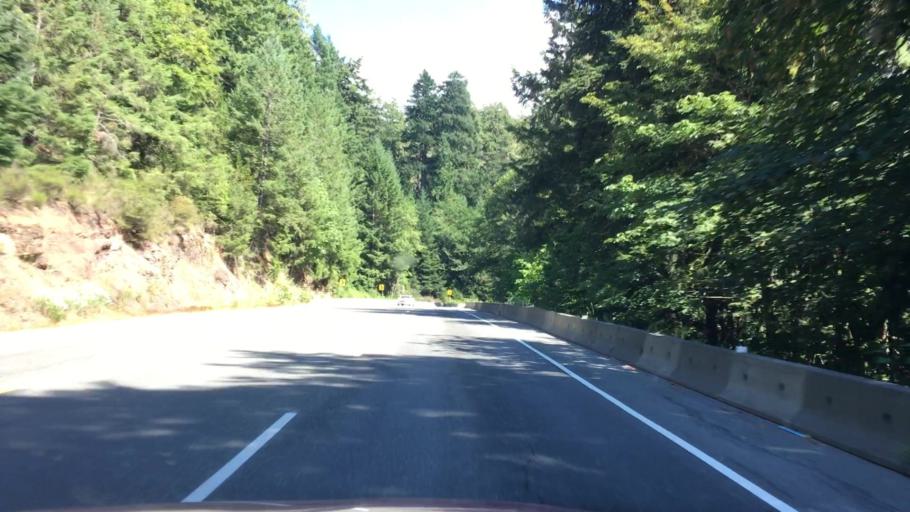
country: CA
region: British Columbia
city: Port Alberni
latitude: 49.2648
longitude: -124.7172
